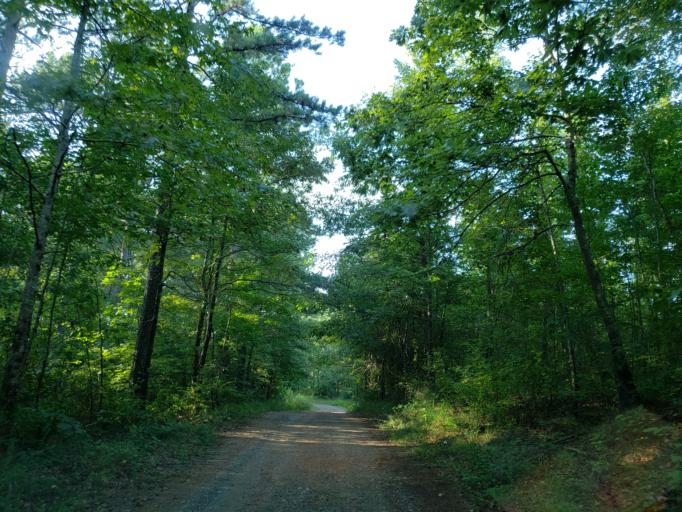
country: US
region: Georgia
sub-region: Cobb County
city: Acworth
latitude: 34.1852
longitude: -84.6463
